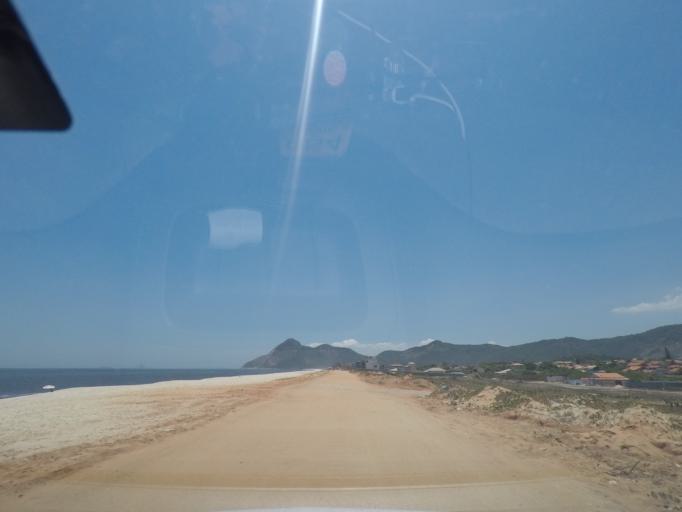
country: BR
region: Rio de Janeiro
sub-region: Niteroi
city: Niteroi
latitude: -22.9694
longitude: -42.9708
